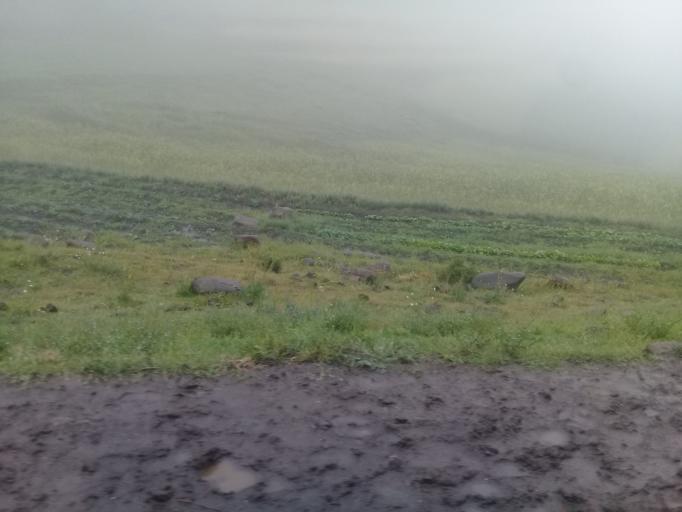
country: LS
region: Mokhotlong
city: Mokhotlong
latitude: -29.3889
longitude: 28.9737
